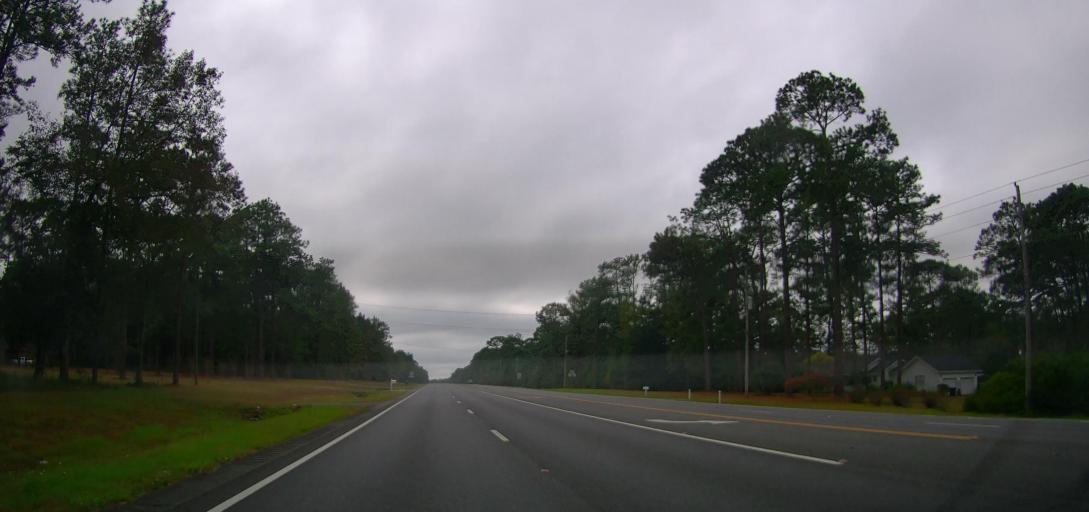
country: US
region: Georgia
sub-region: Thomas County
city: Thomasville
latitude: 30.9119
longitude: -83.9207
